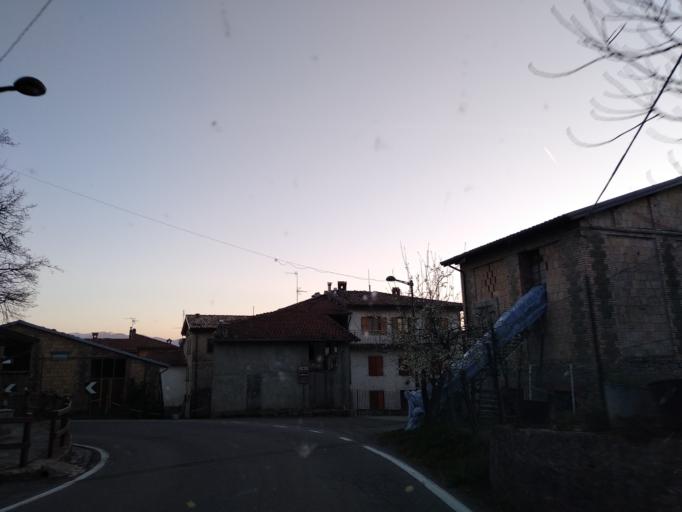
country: IT
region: Emilia-Romagna
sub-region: Provincia di Reggio Emilia
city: Castelnovo ne'Monti
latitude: 44.4150
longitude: 10.4006
